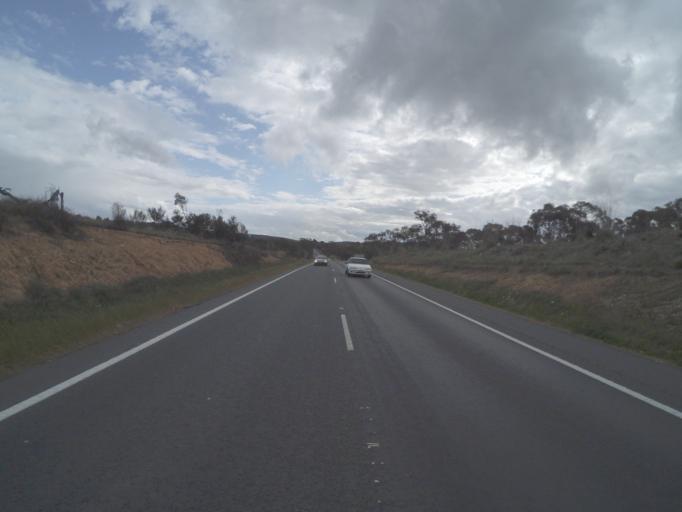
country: AU
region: New South Wales
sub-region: Goulburn Mulwaree
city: Goulburn
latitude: -34.7351
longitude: 149.7927
